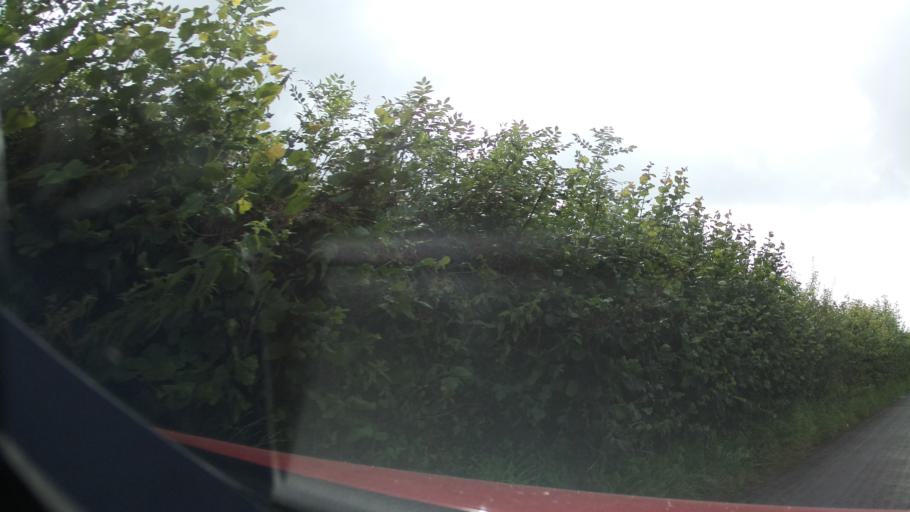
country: GB
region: England
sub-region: Somerset
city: Evercreech
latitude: 51.1674
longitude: -2.5060
